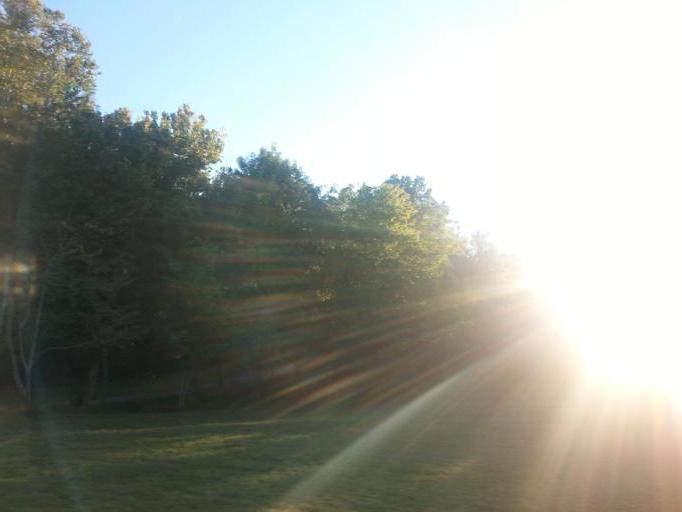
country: US
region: Tennessee
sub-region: Blount County
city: Wildwood
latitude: 35.8946
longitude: -83.8534
